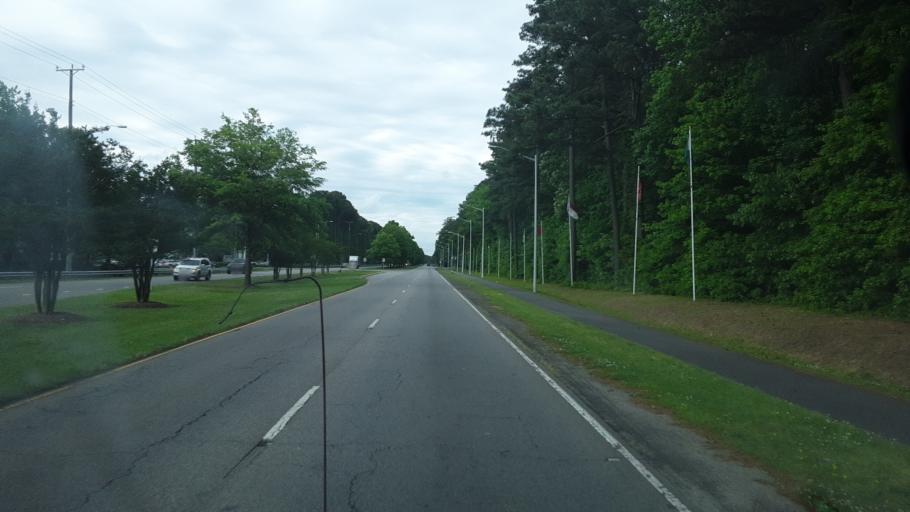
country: US
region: Virginia
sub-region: City of Virginia Beach
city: Virginia Beach
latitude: 36.8093
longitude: -75.9904
